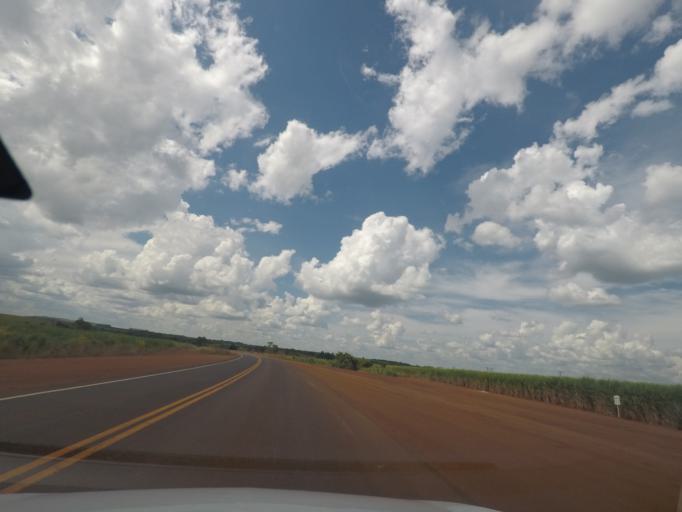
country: BR
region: Minas Gerais
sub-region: Conceicao Das Alagoas
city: Conceicao das Alagoas
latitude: -19.8054
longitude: -48.5806
